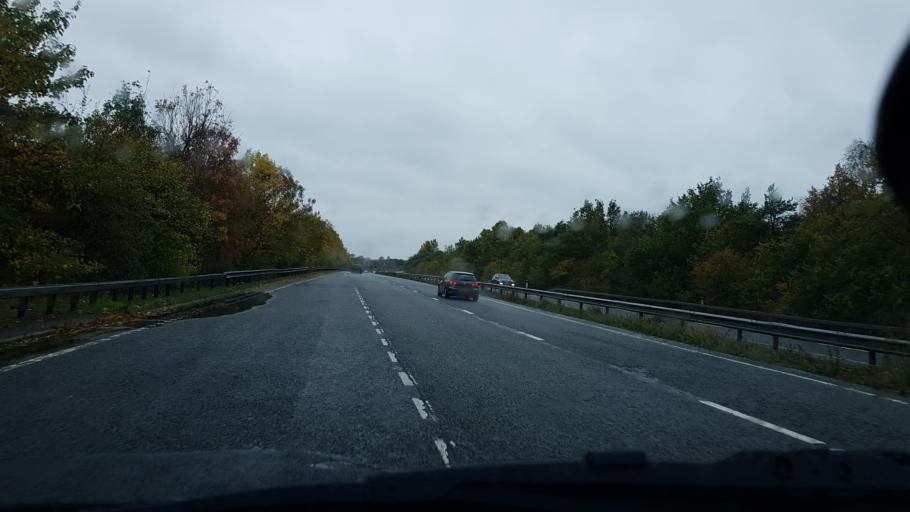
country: GB
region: England
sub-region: Oxfordshire
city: Witney
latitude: 51.7753
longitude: -1.4918
